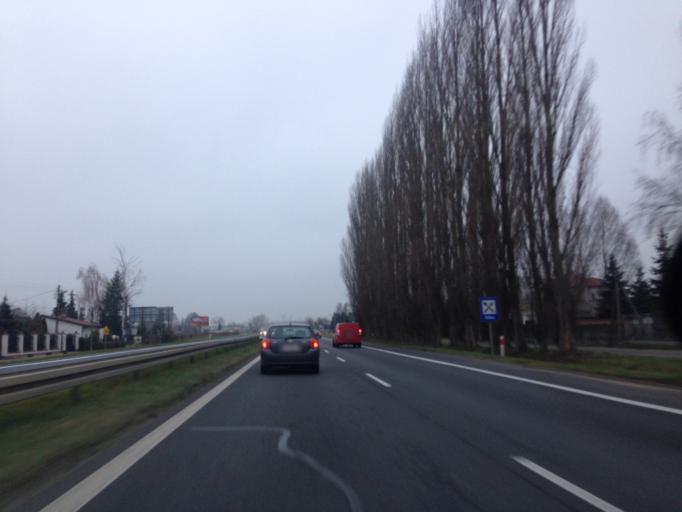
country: PL
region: Lodz Voivodeship
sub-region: Powiat lodzki wschodni
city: Starowa Gora
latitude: 51.6957
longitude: 19.4782
